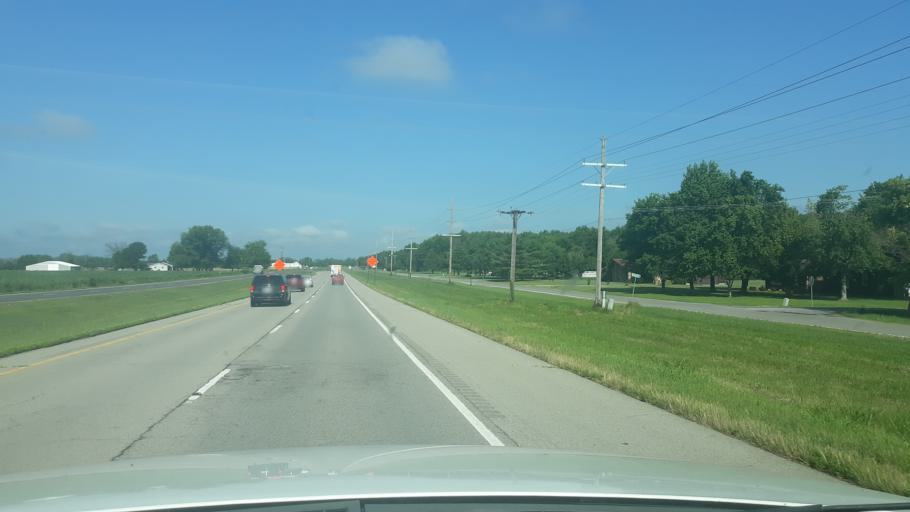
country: US
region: Illinois
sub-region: Williamson County
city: Marion
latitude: 37.7295
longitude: -88.8685
